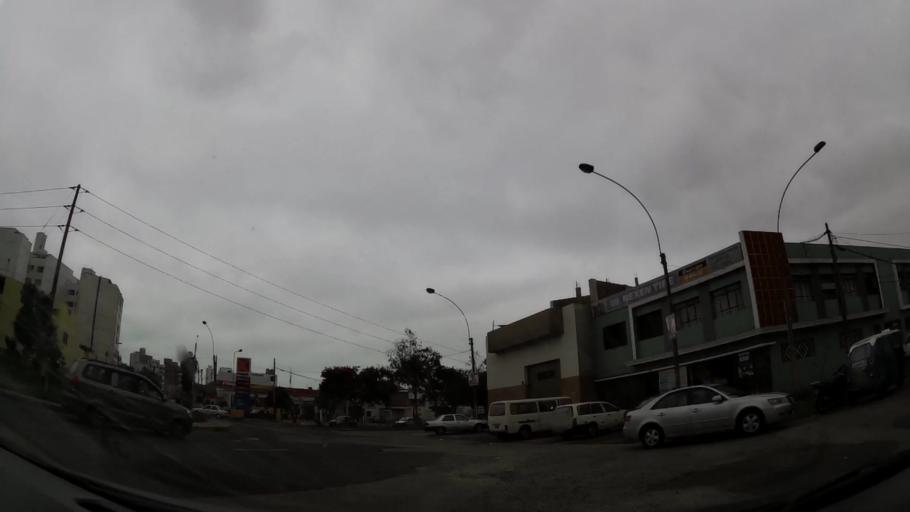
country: PE
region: Lima
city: Lima
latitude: -12.0663
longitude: -77.0542
